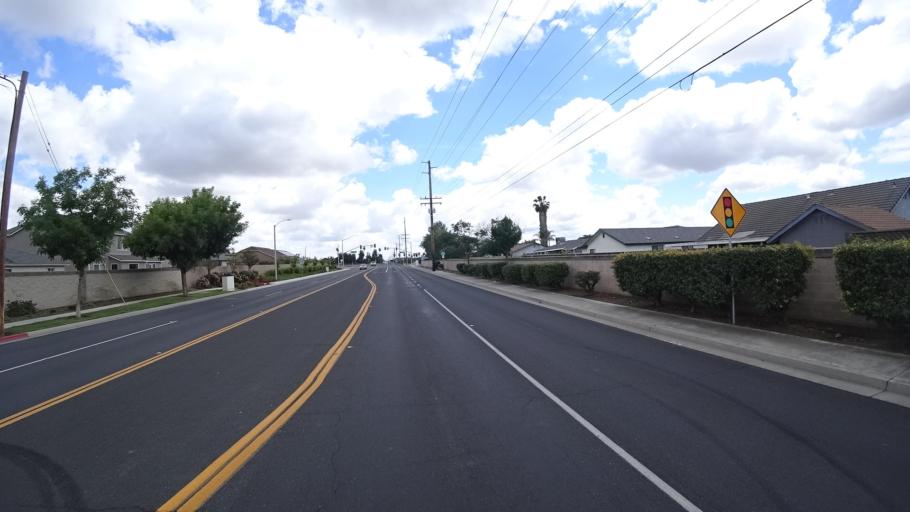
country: US
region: California
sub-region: Kings County
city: Hanford
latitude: 36.3425
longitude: -119.6249
